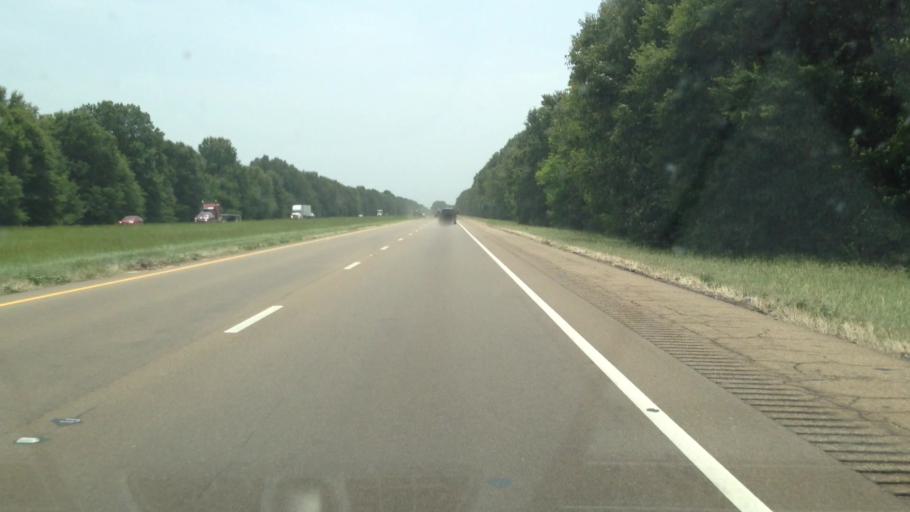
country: US
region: Texas
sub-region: Morris County
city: Naples
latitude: 33.3310
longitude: -94.6740
